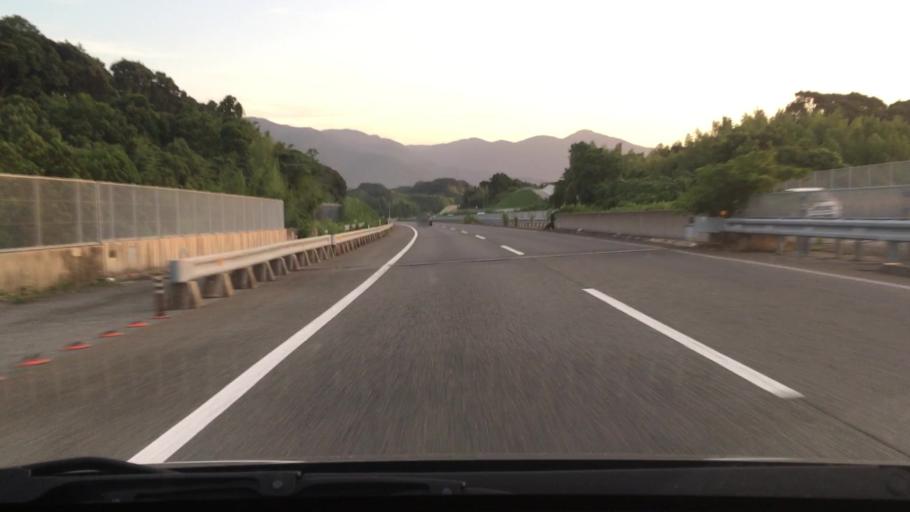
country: JP
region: Fukuoka
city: Maebaru-chuo
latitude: 33.5394
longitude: 130.1979
